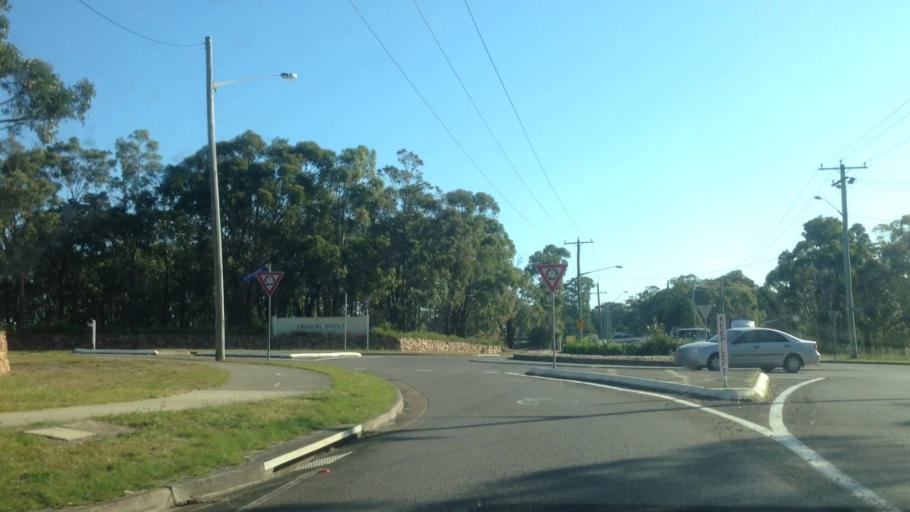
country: AU
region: New South Wales
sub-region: Lake Macquarie Shire
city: Dora Creek
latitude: -33.1088
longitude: 151.5346
